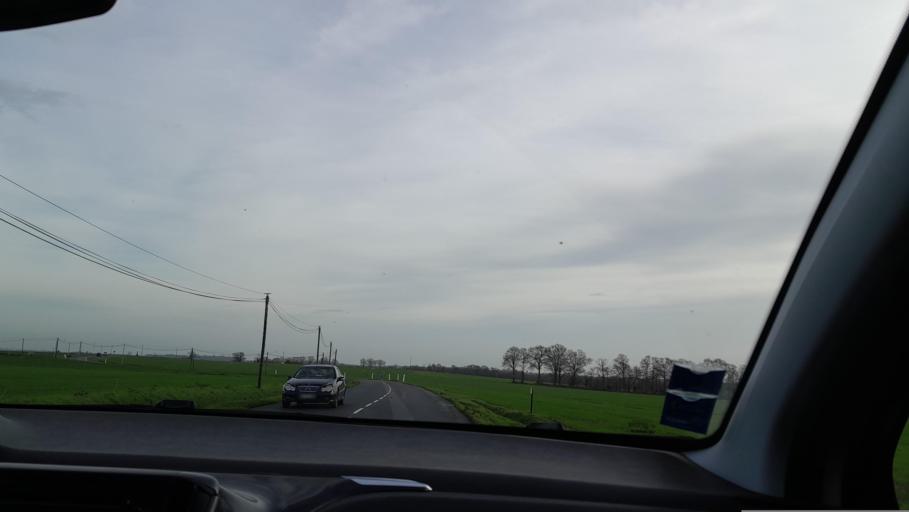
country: FR
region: Brittany
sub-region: Departement d'Ille-et-Vilaine
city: La Guerche-de-Bretagne
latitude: 47.9566
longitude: -1.1730
